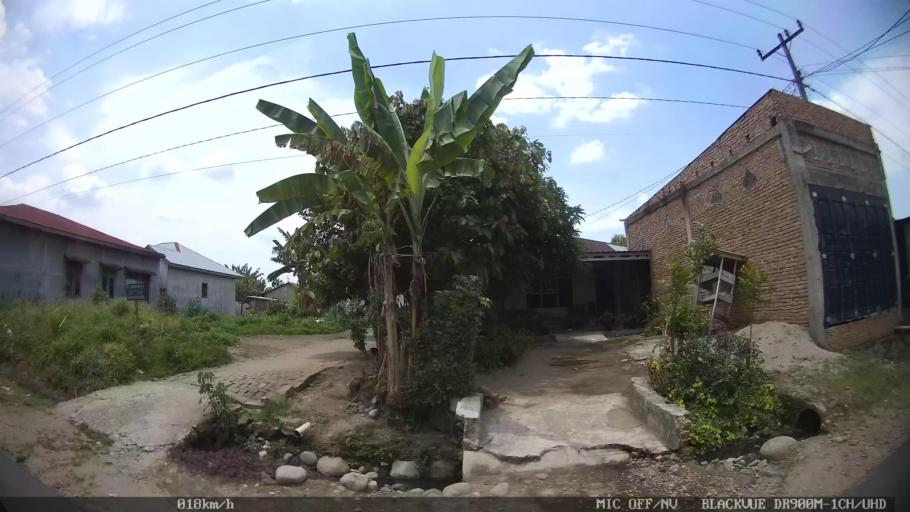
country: ID
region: North Sumatra
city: Binjai
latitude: 3.5894
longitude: 98.5499
